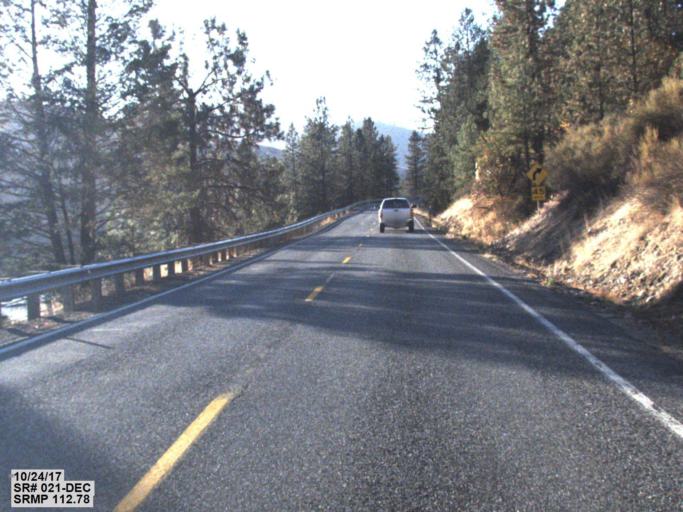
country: US
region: Washington
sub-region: Okanogan County
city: Coulee Dam
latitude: 48.0260
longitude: -118.6721
